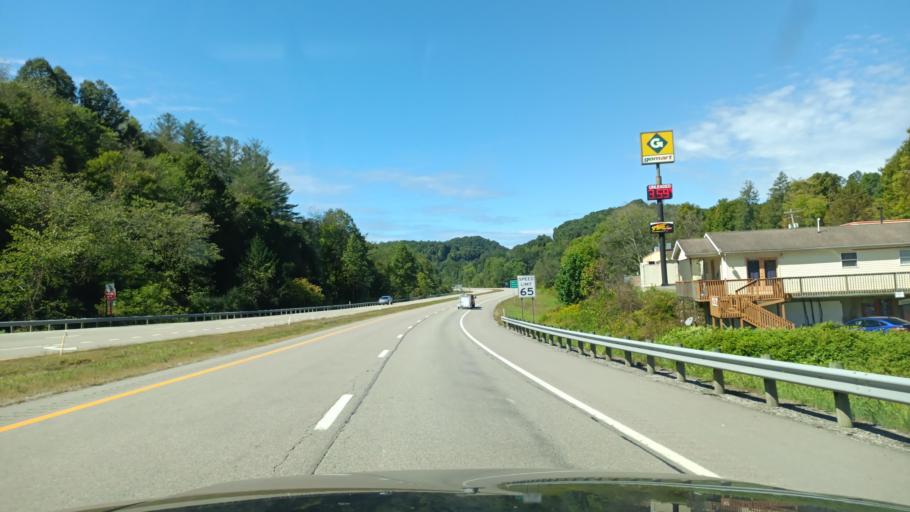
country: US
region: West Virginia
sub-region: Harrison County
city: Salem
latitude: 39.2944
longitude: -80.5682
